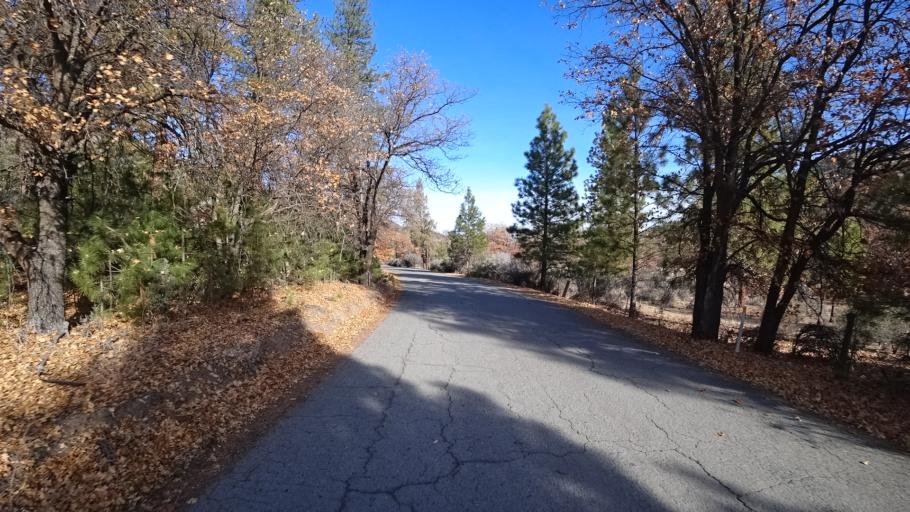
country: US
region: California
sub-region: Siskiyou County
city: Montague
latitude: 41.6110
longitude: -122.5774
